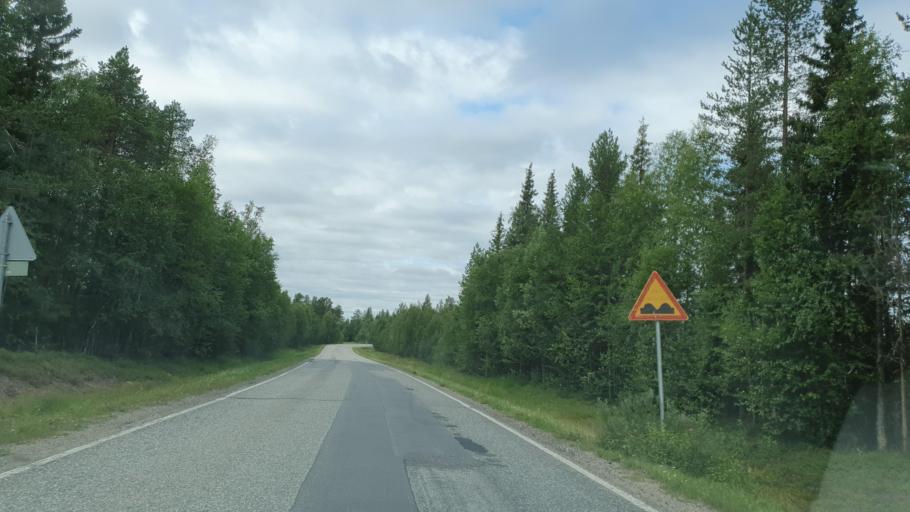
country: FI
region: Lapland
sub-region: Tunturi-Lappi
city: Kittilae
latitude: 67.6113
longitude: 25.2158
